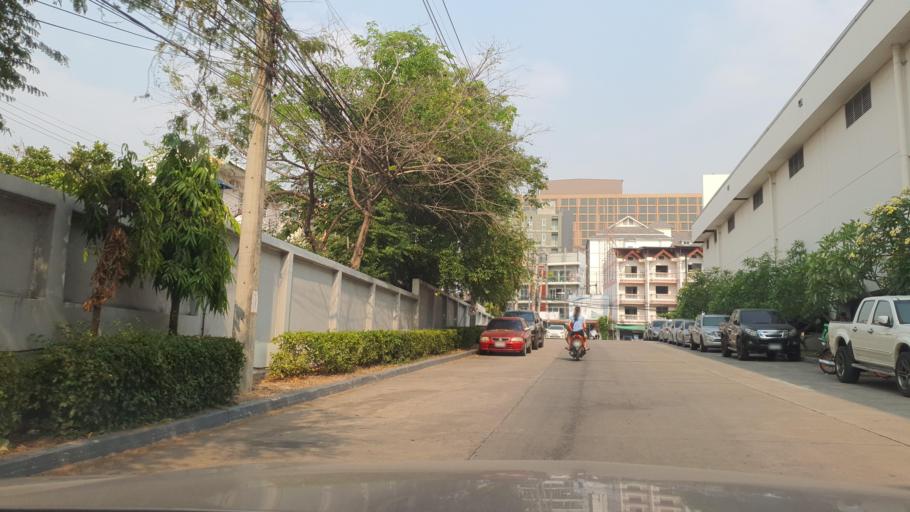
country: TH
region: Chon Buri
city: Phatthaya
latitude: 12.9357
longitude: 100.8951
